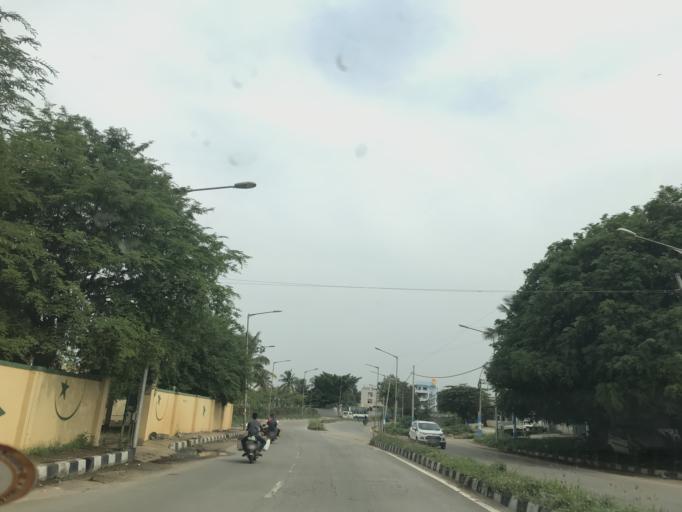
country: IN
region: Karnataka
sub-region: Bangalore Urban
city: Yelahanka
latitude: 13.1304
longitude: 77.6474
